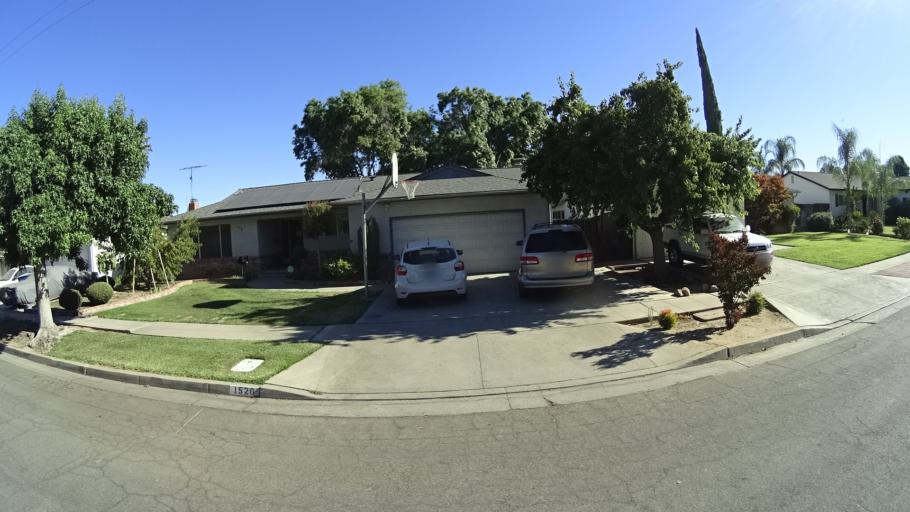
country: US
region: California
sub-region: Fresno County
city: Fresno
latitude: 36.7980
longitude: -119.8290
